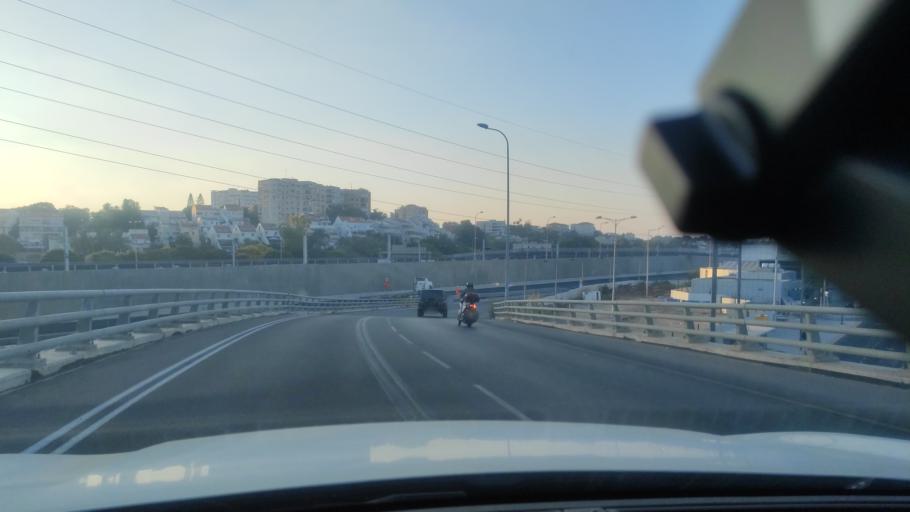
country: IL
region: Tel Aviv
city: Herzliyya
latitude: 32.1625
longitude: 34.8181
